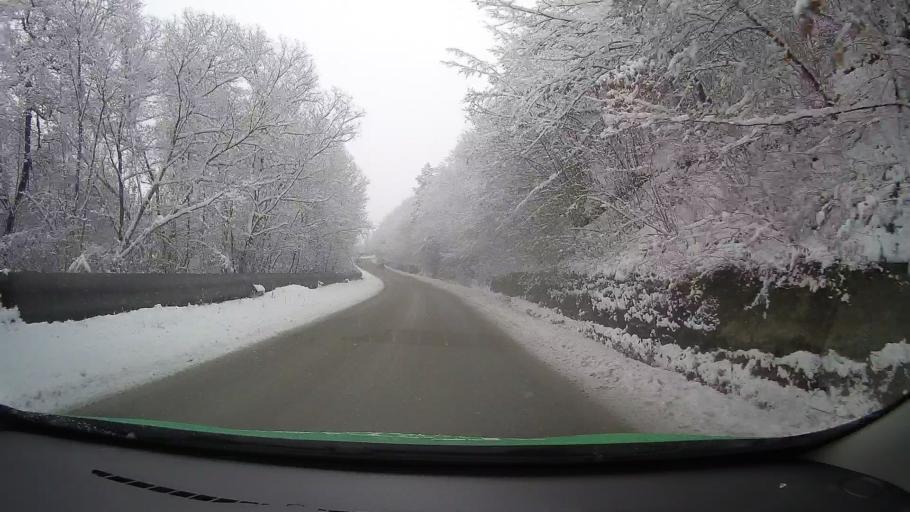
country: RO
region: Hunedoara
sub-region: Comuna Teliucu Inferior
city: Teliucu Inferior
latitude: 45.7236
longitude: 22.8798
